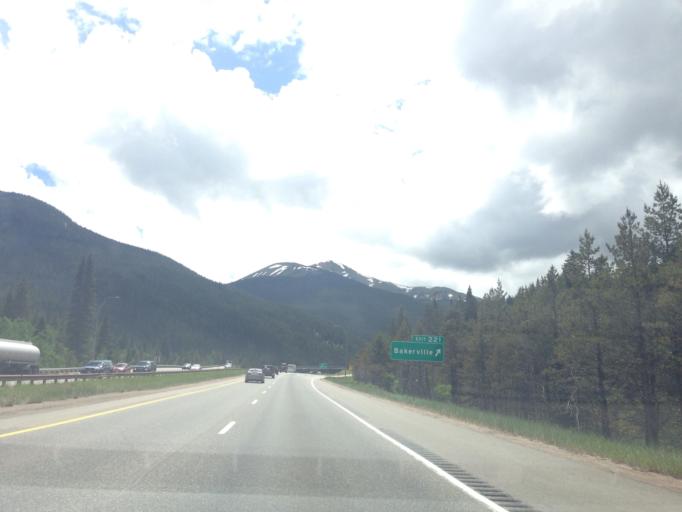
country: US
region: Colorado
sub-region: Clear Creek County
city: Georgetown
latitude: 39.6941
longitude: -105.8000
